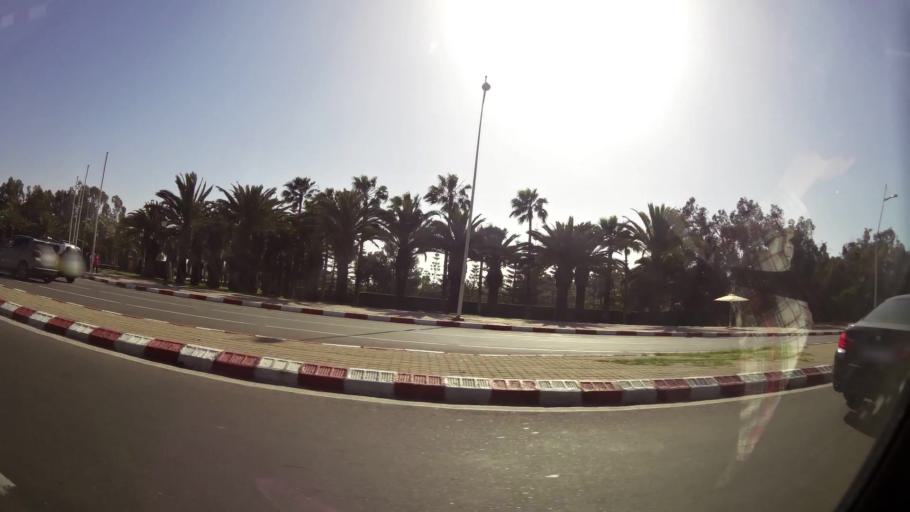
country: MA
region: Oued ed Dahab-Lagouira
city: Dakhla
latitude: 30.3906
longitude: -9.5763
